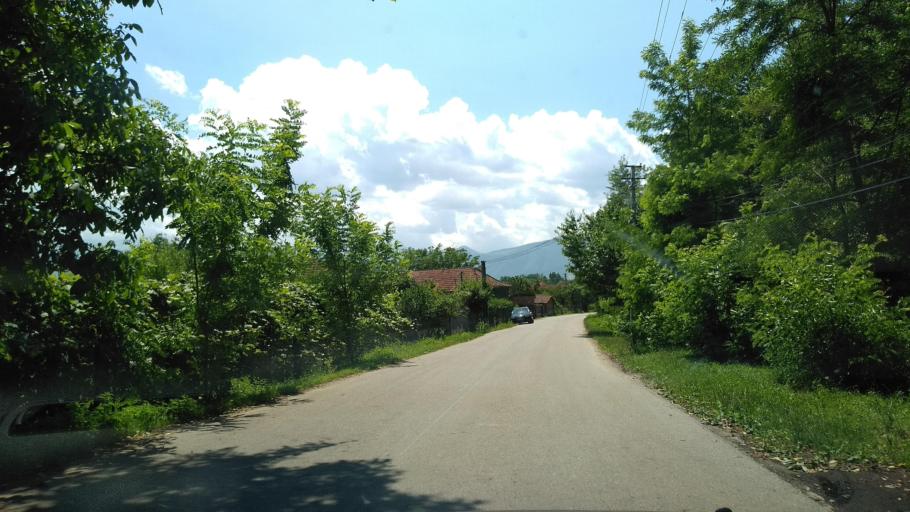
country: RO
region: Hunedoara
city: Densus
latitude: 45.5535
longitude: 22.8230
